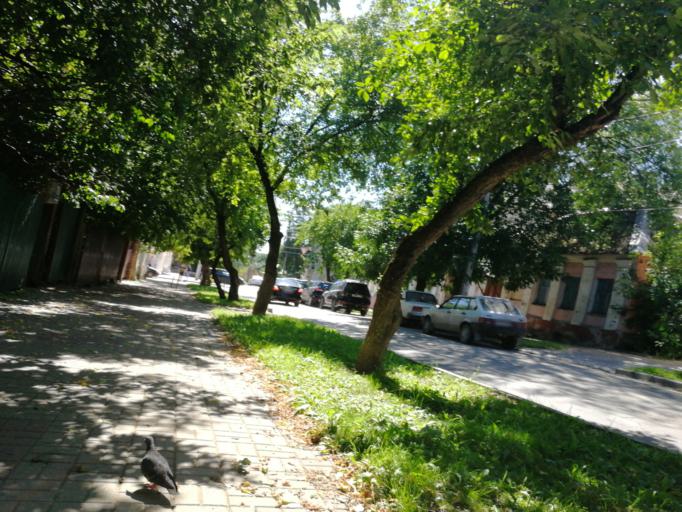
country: RU
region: Kaluga
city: Kaluga
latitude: 54.5058
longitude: 36.2569
